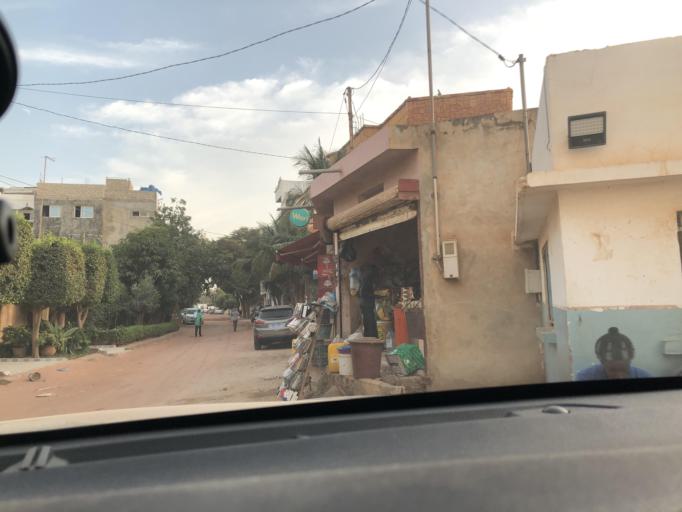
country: SN
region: Dakar
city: Mermoz Boabab
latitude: 14.7289
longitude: -17.5020
